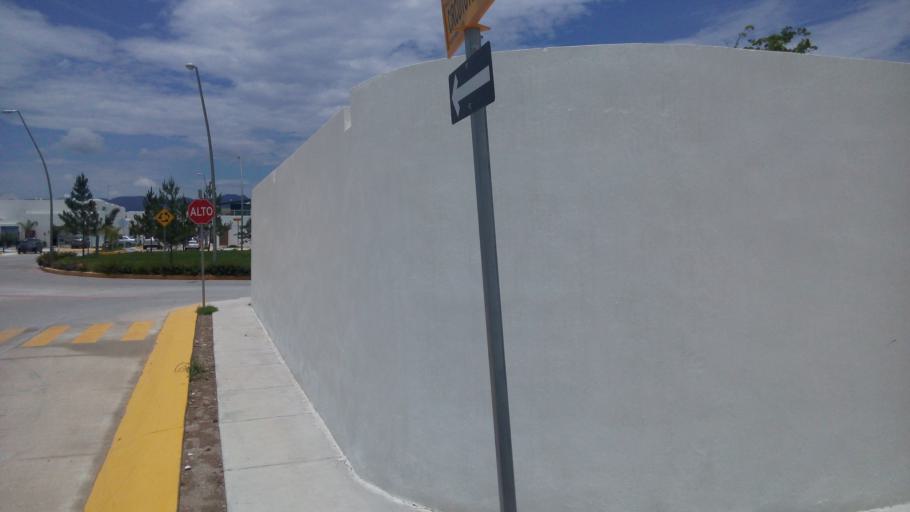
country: MX
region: Aguascalientes
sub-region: Aguascalientes
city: San Sebastian [Fraccionamiento]
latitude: 21.8318
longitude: -102.3176
